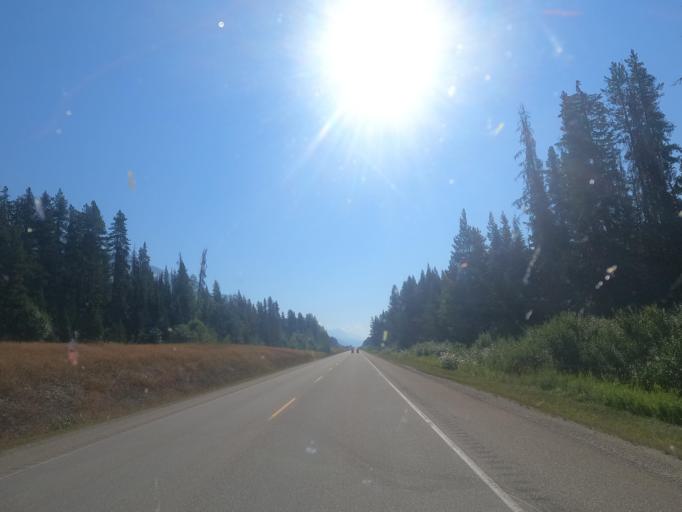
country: CA
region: Alberta
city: Grande Cache
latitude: 52.9892
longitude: -119.0063
